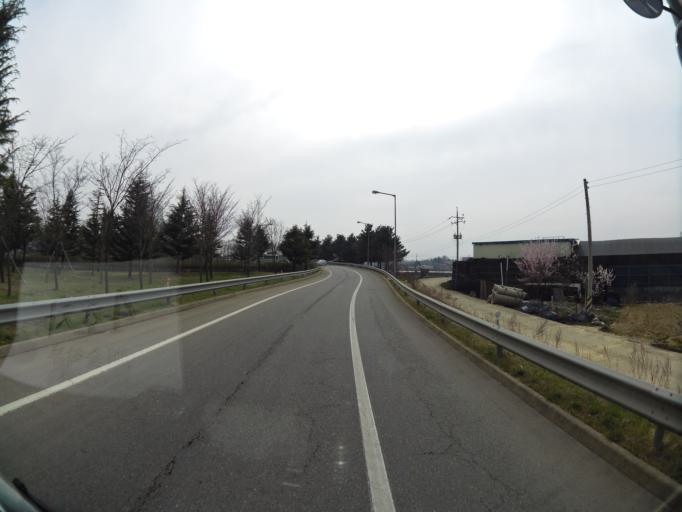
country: KR
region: Gyeongsangbuk-do
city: Hayang
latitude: 35.8738
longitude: 128.7948
